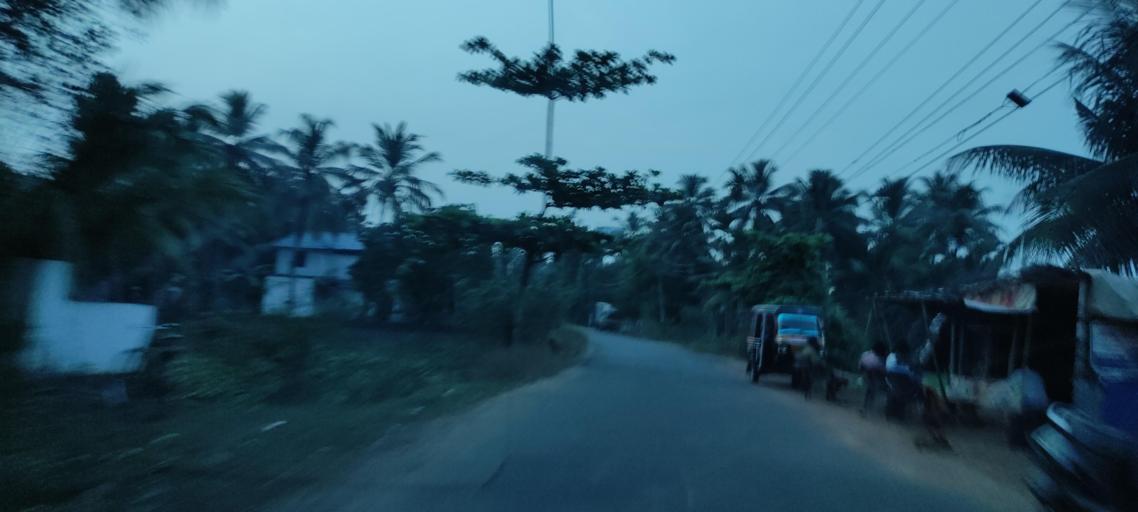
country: IN
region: Kerala
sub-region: Alappuzha
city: Mavelikara
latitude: 9.3310
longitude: 76.4762
